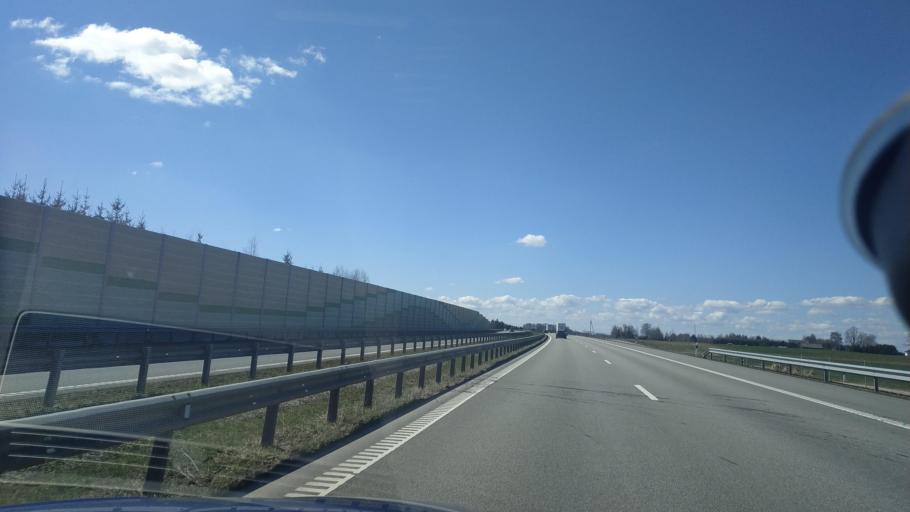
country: LT
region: Kauno apskritis
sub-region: Kauno rajonas
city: Mastaiciai
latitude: 54.7592
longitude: 23.7408
